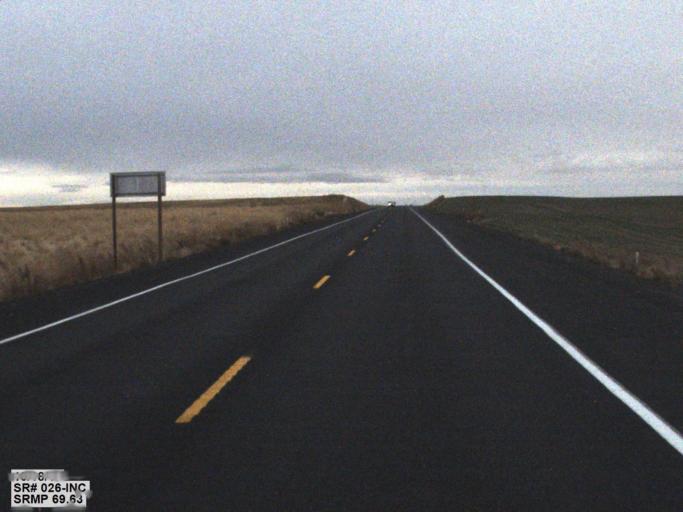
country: US
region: Washington
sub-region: Franklin County
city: Connell
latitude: 46.7947
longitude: -118.5676
